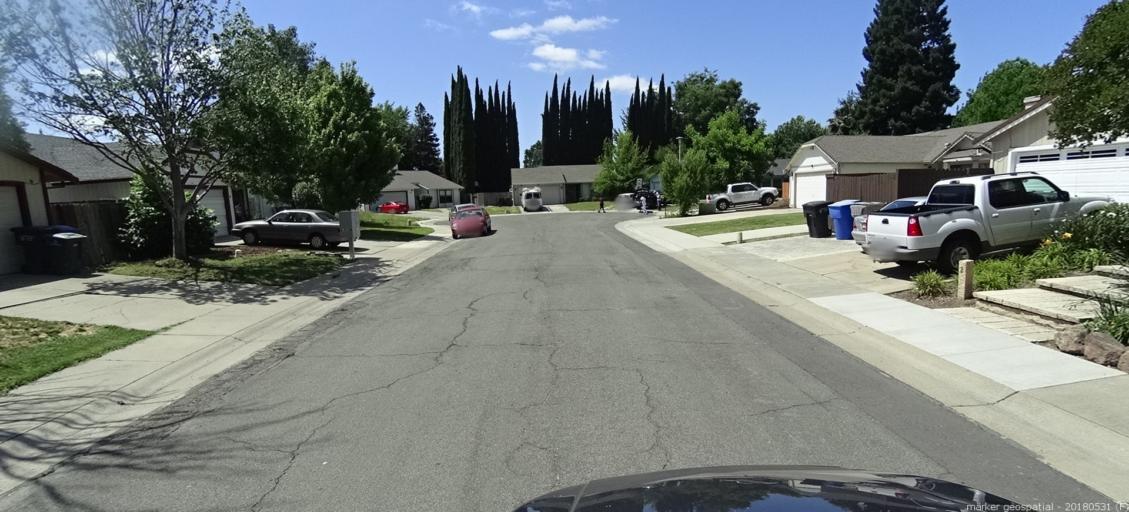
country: US
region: California
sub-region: Sacramento County
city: Sacramento
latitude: 38.6246
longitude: -121.4998
